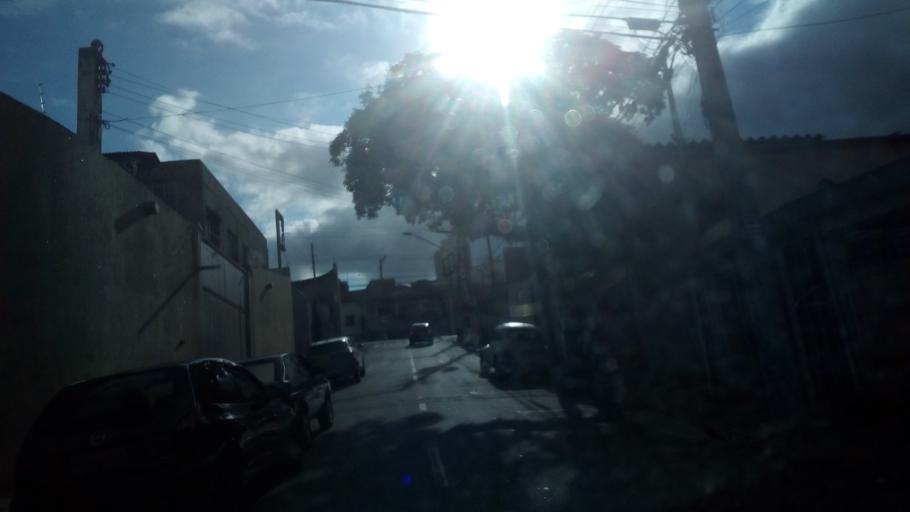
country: BR
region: Sao Paulo
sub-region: Guarulhos
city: Guarulhos
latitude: -23.4612
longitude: -46.5197
